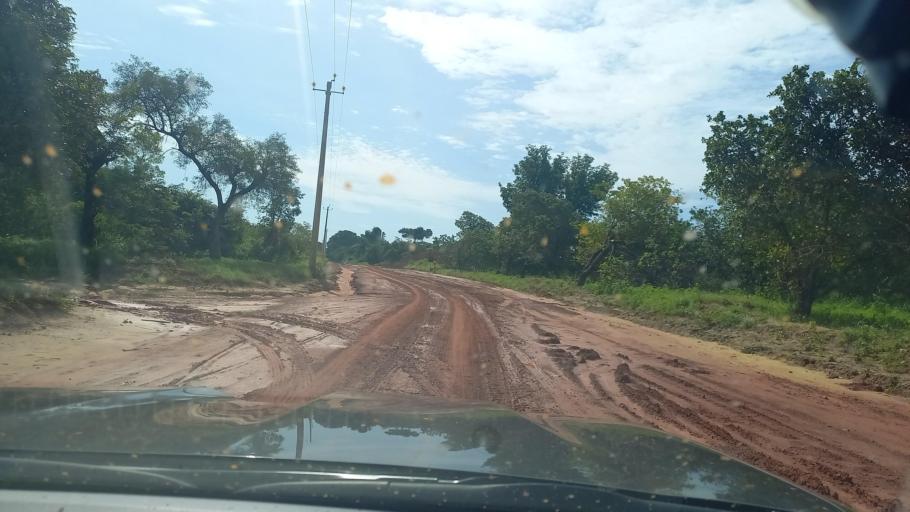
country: SN
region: Ziguinchor
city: Ziguinchor
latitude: 12.6713
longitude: -16.1898
